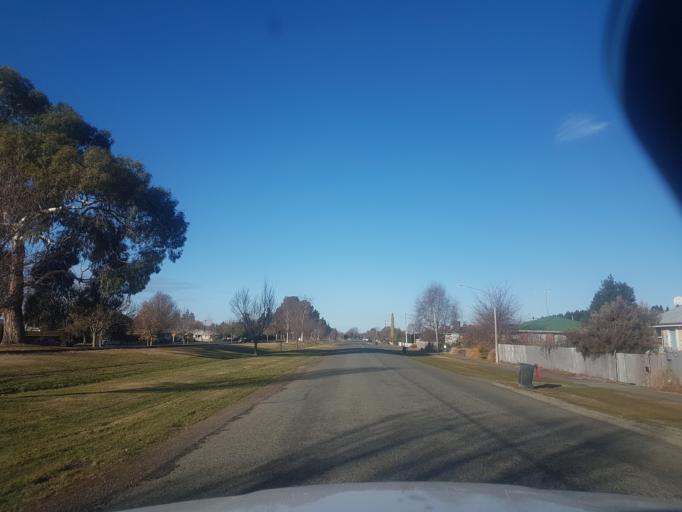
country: NZ
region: Canterbury
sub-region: Timaru District
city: Pleasant Point
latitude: -44.2622
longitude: 171.1340
